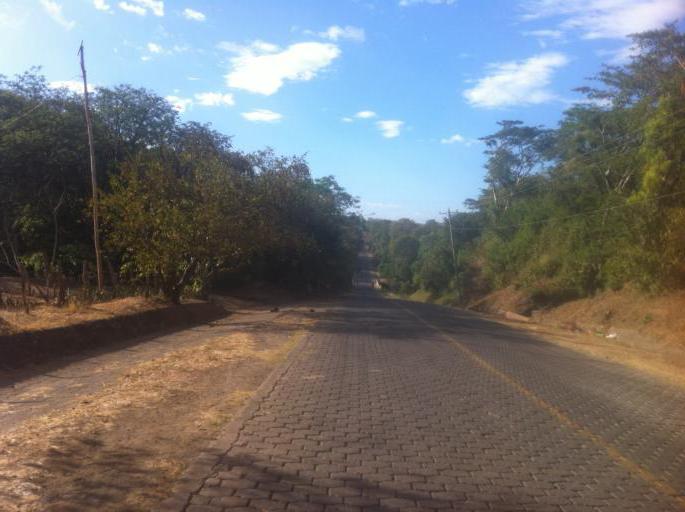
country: NI
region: Managua
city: Masachapa
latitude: 11.8229
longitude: -86.4978
